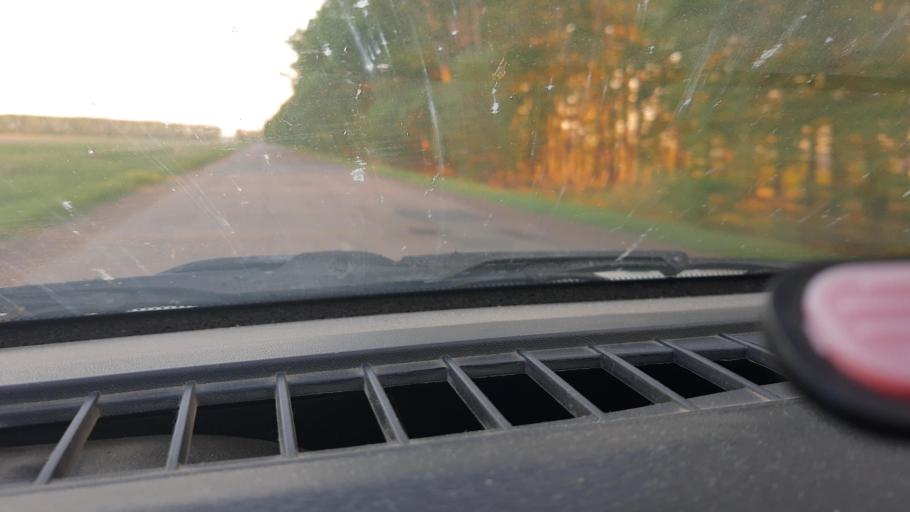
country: RU
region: Bashkortostan
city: Asanovo
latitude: 54.8273
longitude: 55.5978
